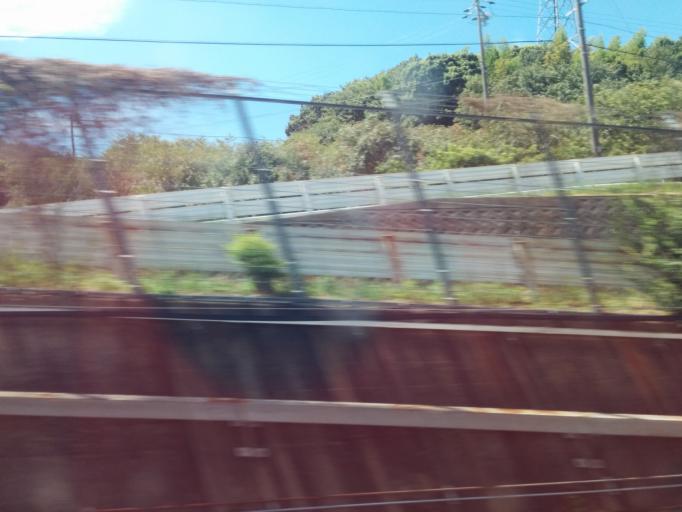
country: JP
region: Aichi
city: Gamagori
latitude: 34.8532
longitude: 137.1767
